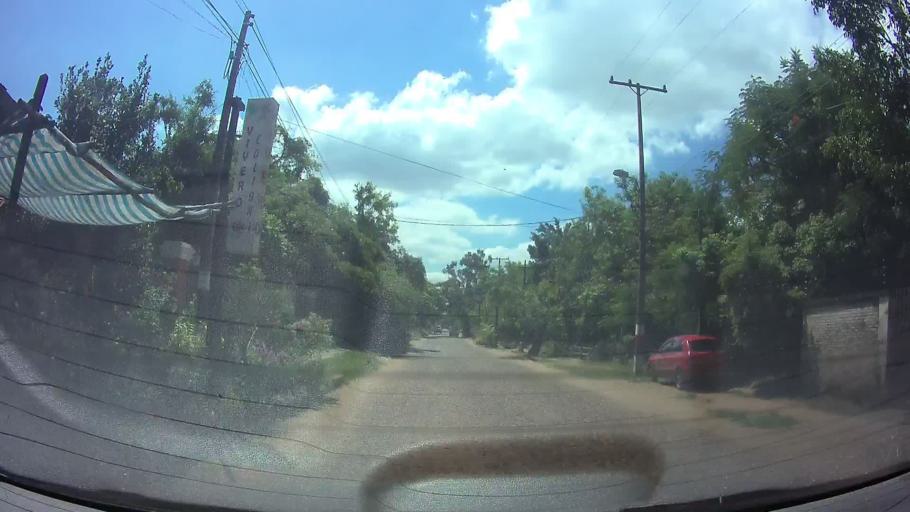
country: PY
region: Central
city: Aregua
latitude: -25.3080
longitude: -57.3841
